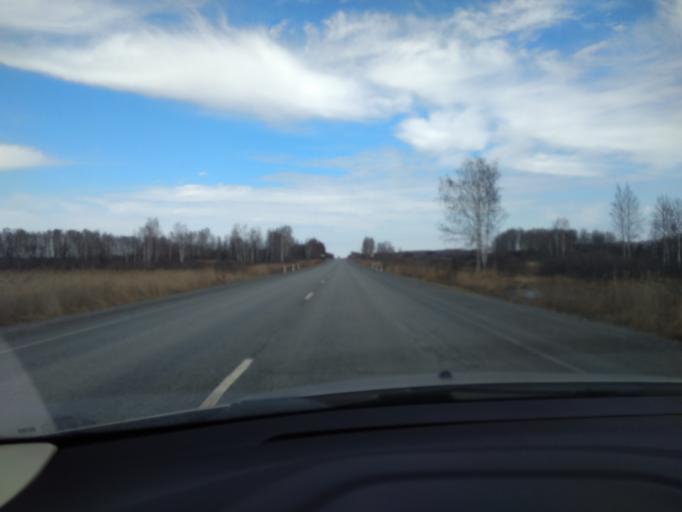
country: RU
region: Sverdlovsk
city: Pyshma
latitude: 57.0031
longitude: 63.3197
